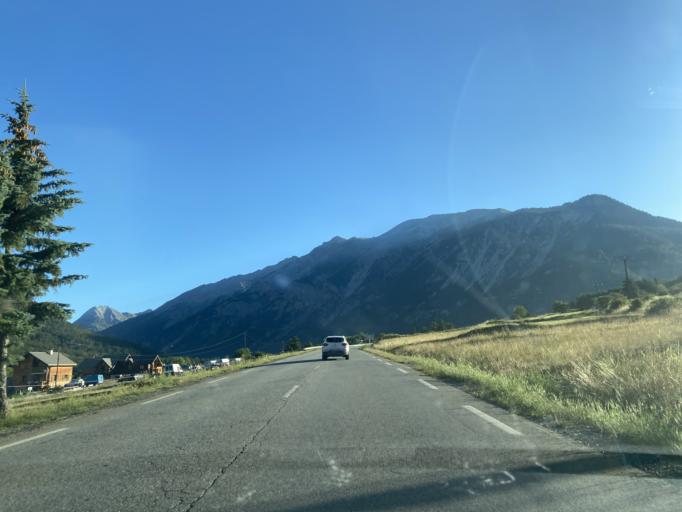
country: FR
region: Provence-Alpes-Cote d'Azur
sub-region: Departement des Hautes-Alpes
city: Briancon
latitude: 44.9174
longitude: 6.6767
